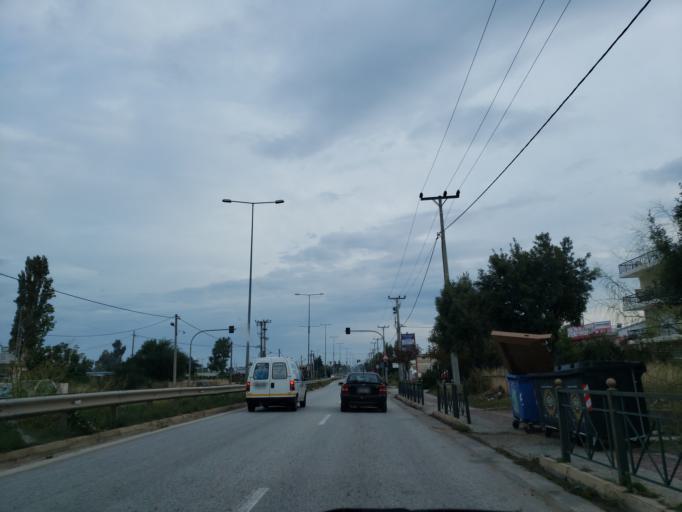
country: GR
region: Attica
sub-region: Nomarchia Anatolikis Attikis
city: Nea Makri
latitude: 38.1023
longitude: 23.9701
